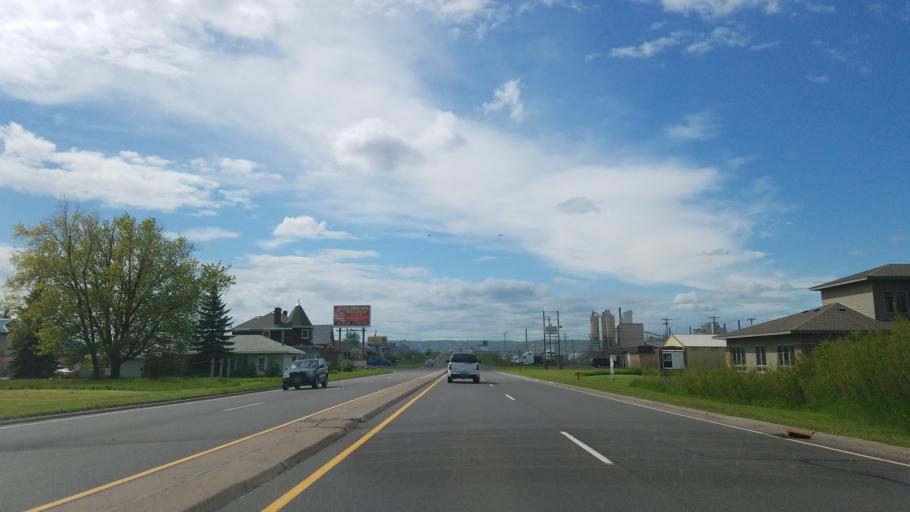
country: US
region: Wisconsin
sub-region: Douglas County
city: Superior
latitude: 46.7243
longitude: -92.0715
